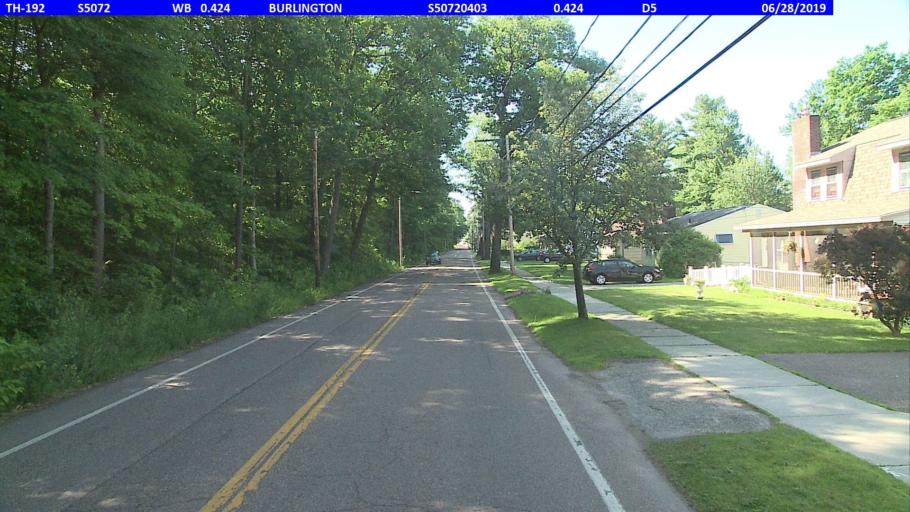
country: US
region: Vermont
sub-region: Chittenden County
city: Burlington
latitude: 44.5097
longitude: -73.2416
